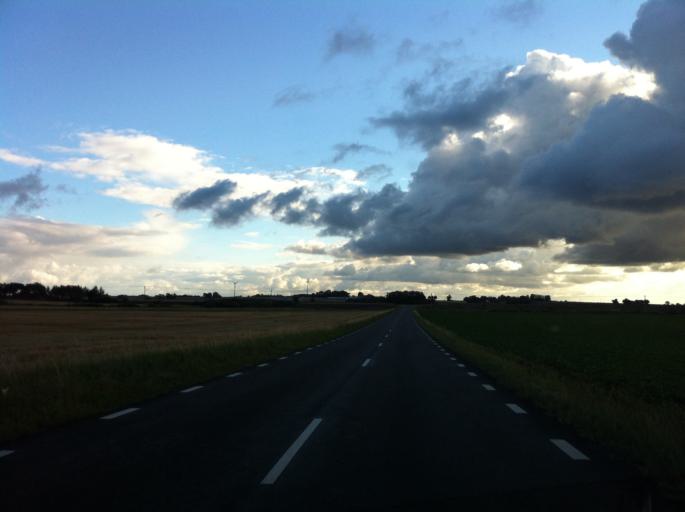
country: SE
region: Skane
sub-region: Svalovs Kommun
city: Svaloev
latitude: 55.9126
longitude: 13.2001
